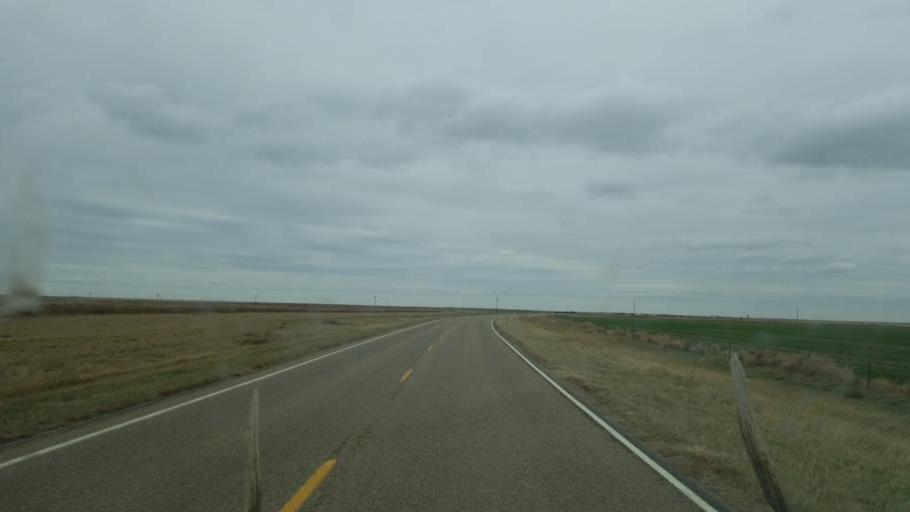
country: US
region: Colorado
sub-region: Cheyenne County
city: Cheyenne Wells
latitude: 38.8524
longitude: -102.2268
